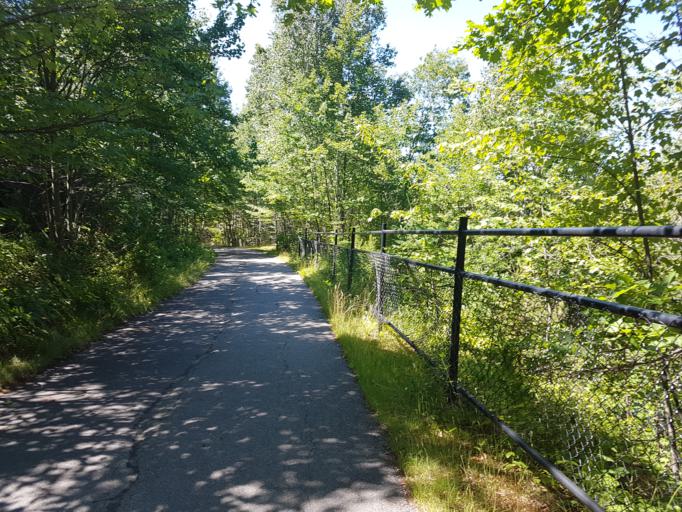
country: CA
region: Quebec
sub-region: Abitibi-Temiscamingue
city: Temiscaming
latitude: 46.7203
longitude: -79.0944
